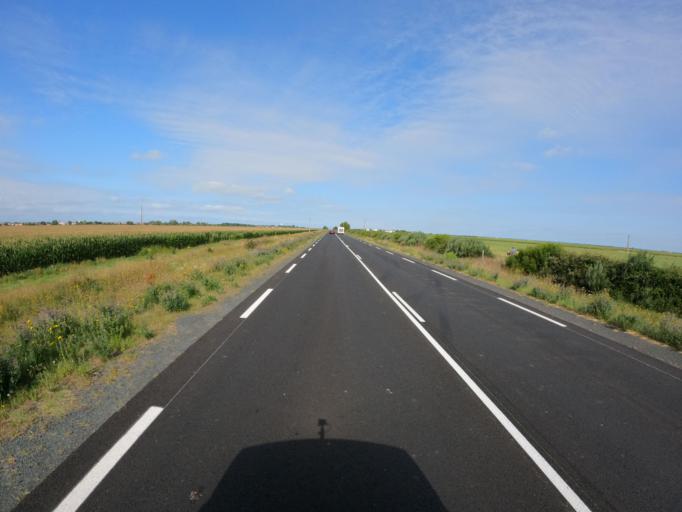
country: FR
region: Pays de la Loire
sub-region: Departement de la Vendee
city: Triaize
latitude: 46.3394
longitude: -1.2867
